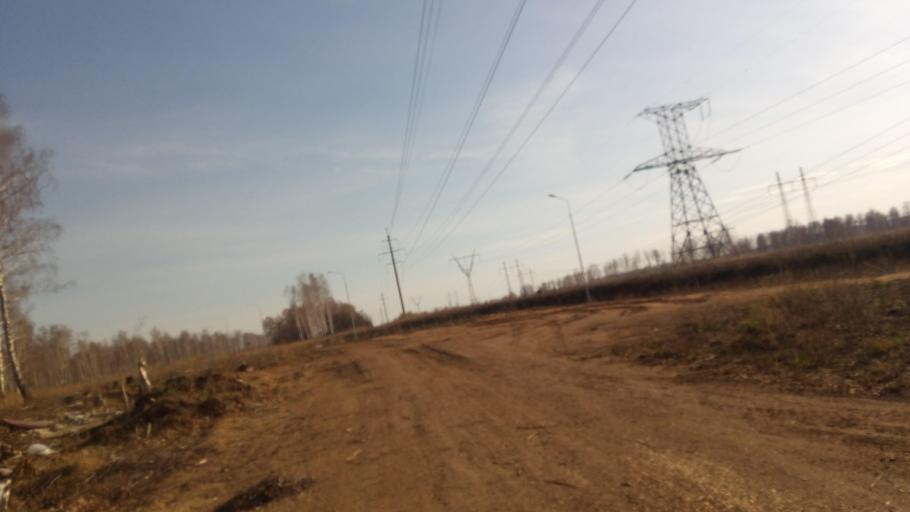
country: RU
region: Chelyabinsk
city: Sargazy
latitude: 55.1157
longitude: 61.2358
